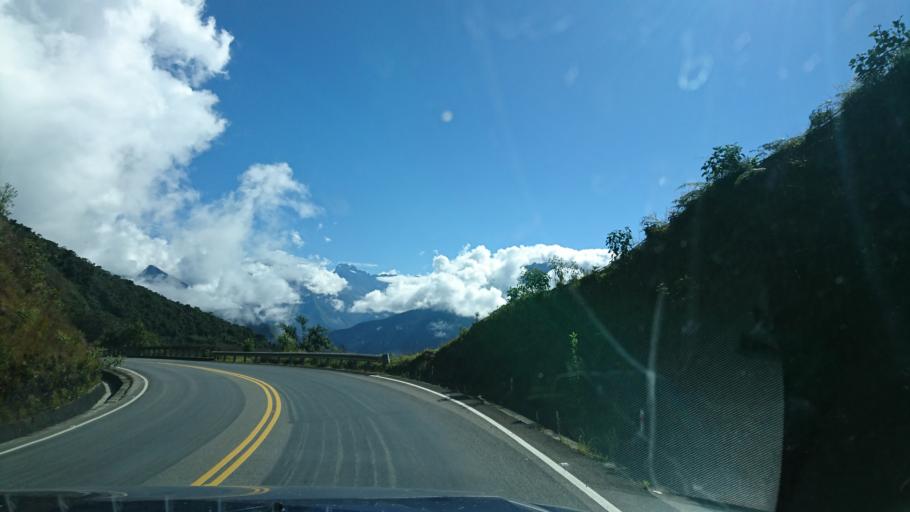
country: BO
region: La Paz
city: Coroico
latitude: -16.2191
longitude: -67.8196
